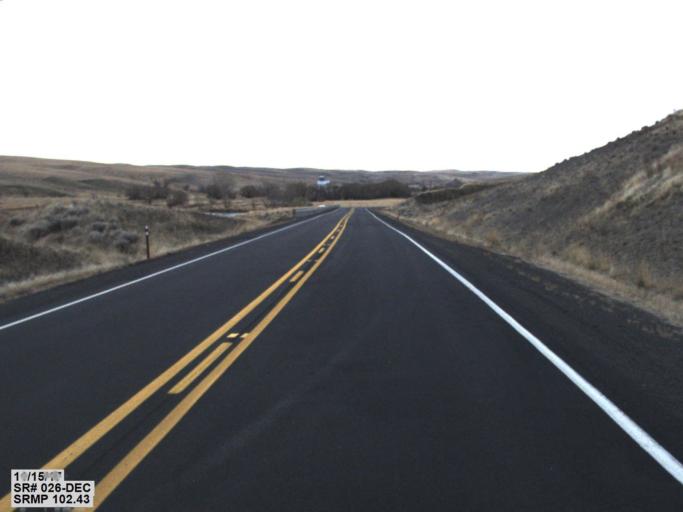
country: US
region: Washington
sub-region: Garfield County
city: Pomeroy
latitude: 46.7839
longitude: -117.9420
